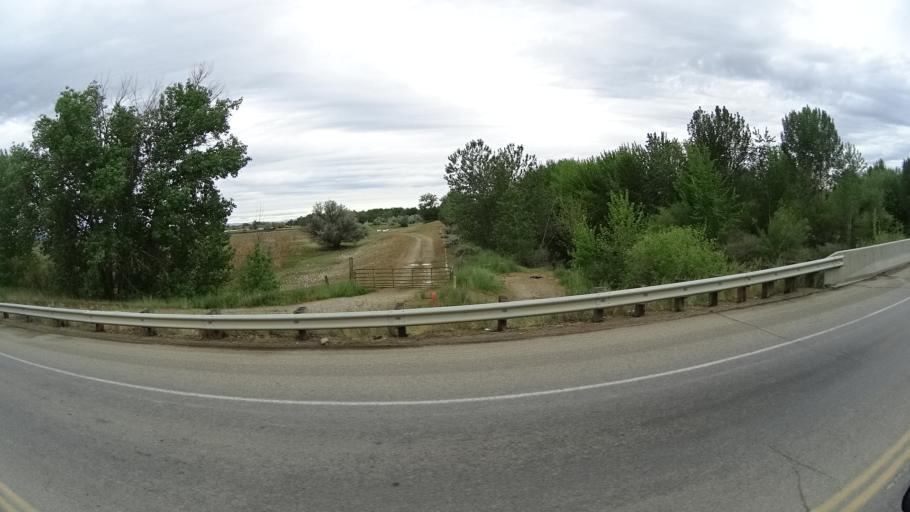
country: US
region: Idaho
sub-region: Ada County
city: Star
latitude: 43.6797
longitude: -116.4932
